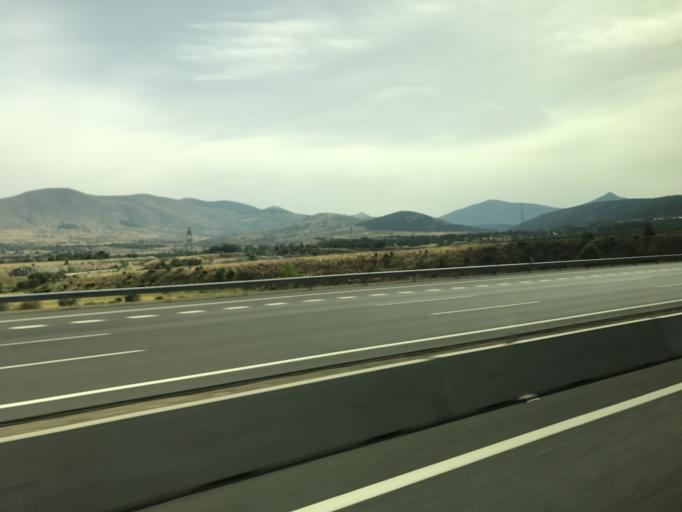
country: ES
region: Castille and Leon
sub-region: Provincia de Segovia
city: Otero de Herreros
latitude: 40.7370
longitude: -4.2114
